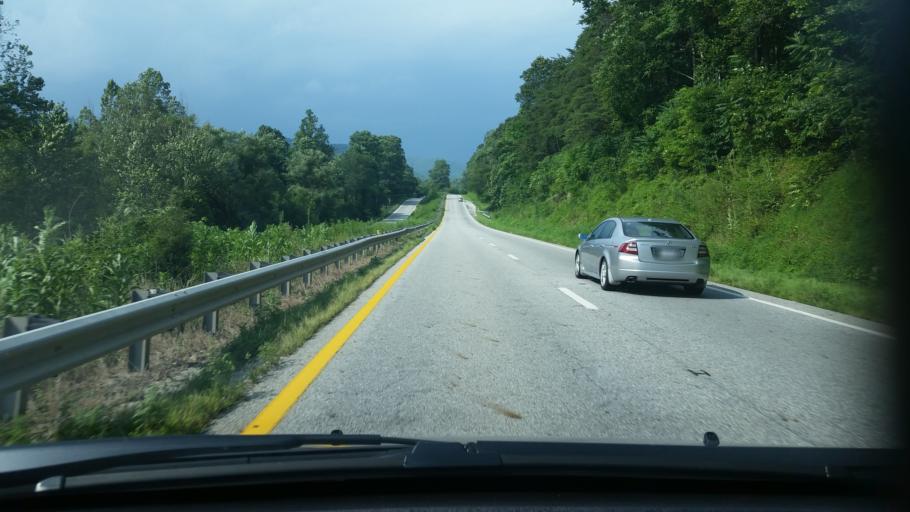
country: US
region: Virginia
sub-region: Nelson County
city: Lovingston
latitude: 37.7877
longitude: -78.8661
